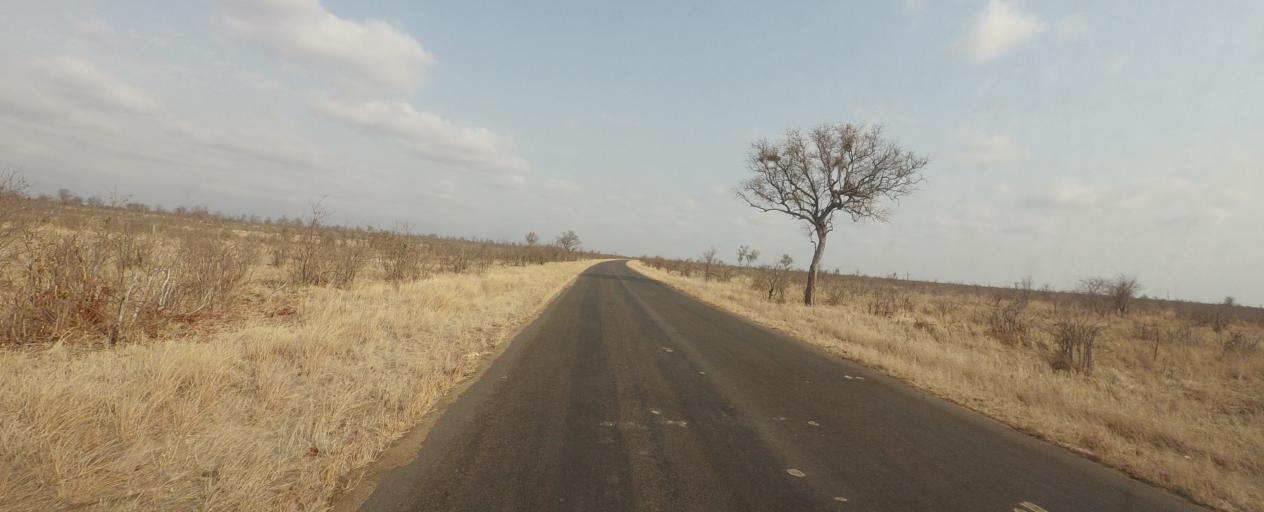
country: ZA
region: Limpopo
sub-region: Vhembe District Municipality
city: Mutale
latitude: -22.9307
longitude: 31.2639
